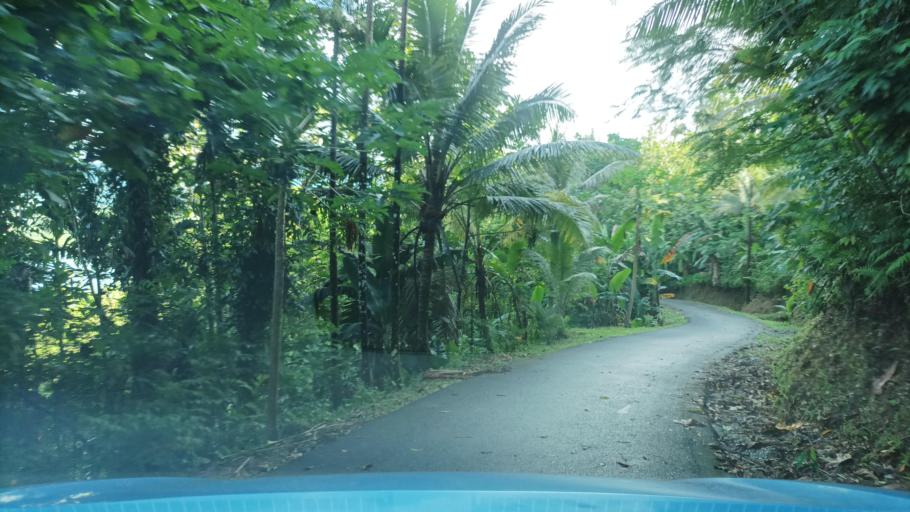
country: FM
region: Pohnpei
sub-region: Kolonia Municipality
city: Kolonia Town
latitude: 6.9623
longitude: 158.1944
